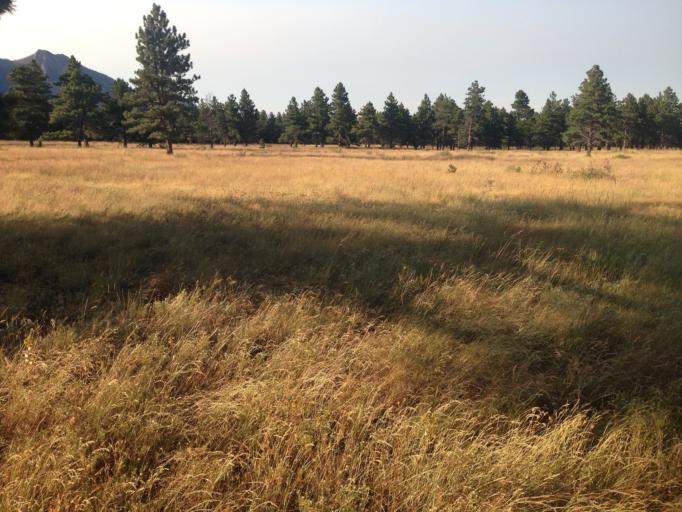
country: US
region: Colorado
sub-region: Boulder County
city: Superior
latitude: 39.9141
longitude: -105.2559
